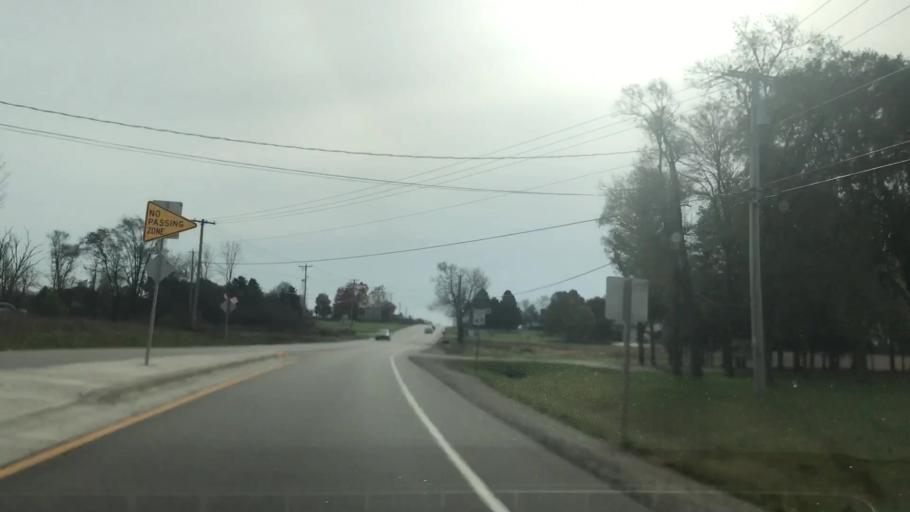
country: US
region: Wisconsin
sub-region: Waukesha County
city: Menomonee Falls
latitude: 43.2056
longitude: -88.1565
